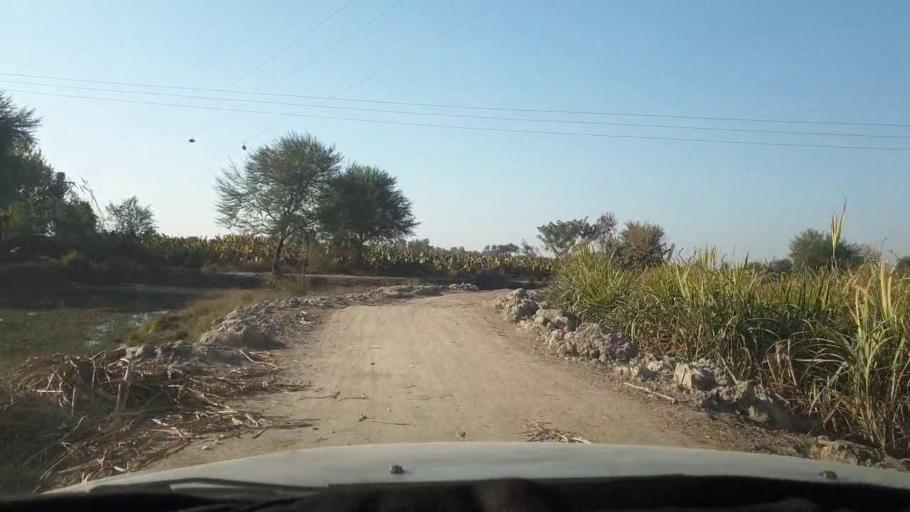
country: PK
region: Sindh
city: Adilpur
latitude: 27.9381
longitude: 69.2579
